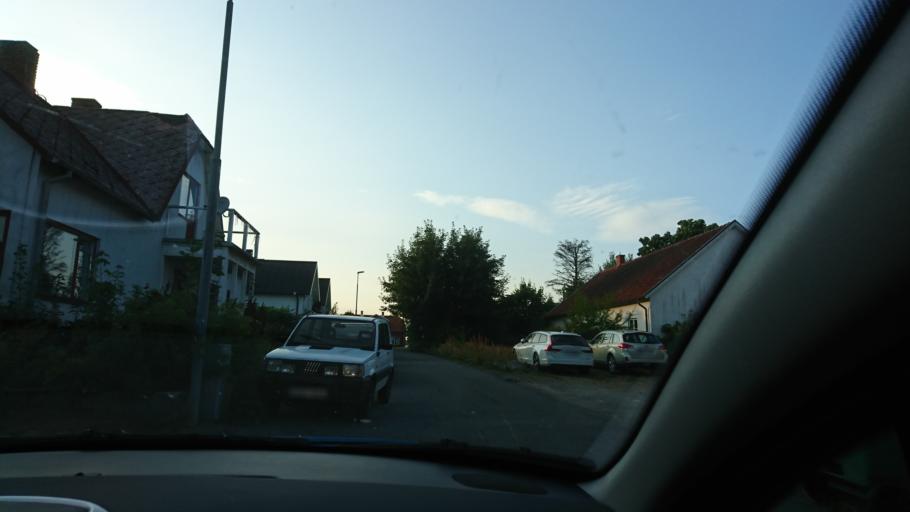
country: SE
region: Skane
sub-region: Simrishamns Kommun
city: Kivik
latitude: 55.6849
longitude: 14.1540
